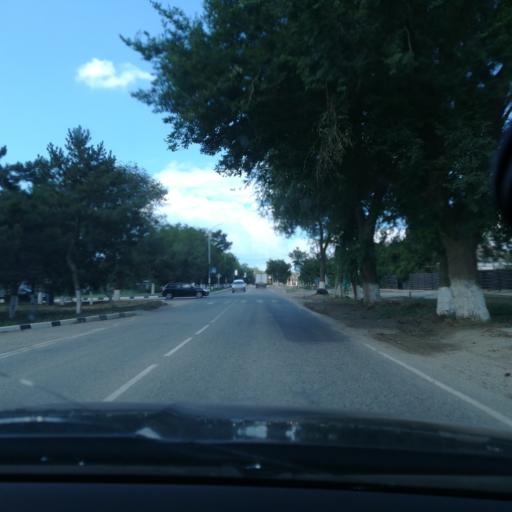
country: RU
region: Krasnodarskiy
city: Taman'
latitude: 45.2177
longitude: 36.7402
